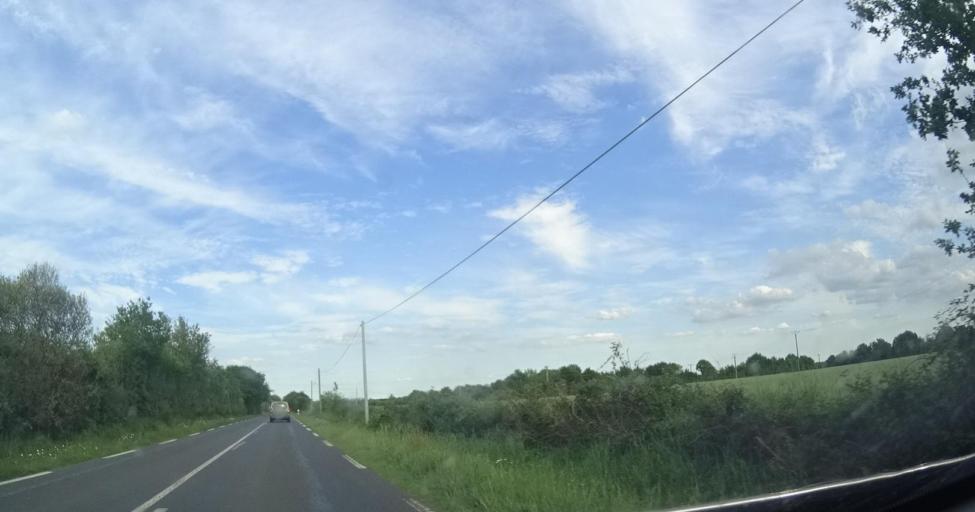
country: FR
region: Pays de la Loire
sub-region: Departement de la Loire-Atlantique
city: Fay-de-Bretagne
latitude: 47.4080
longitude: -1.7471
